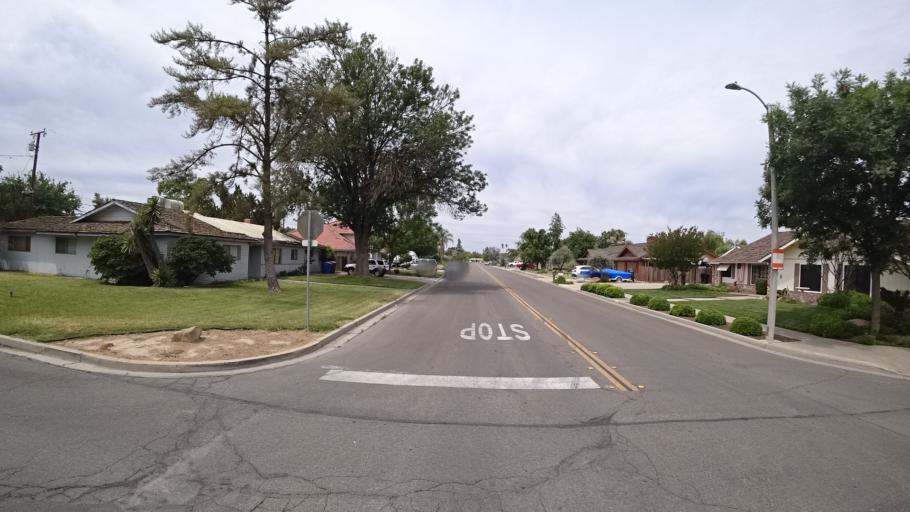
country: US
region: California
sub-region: Kings County
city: Hanford
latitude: 36.3555
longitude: -119.6416
